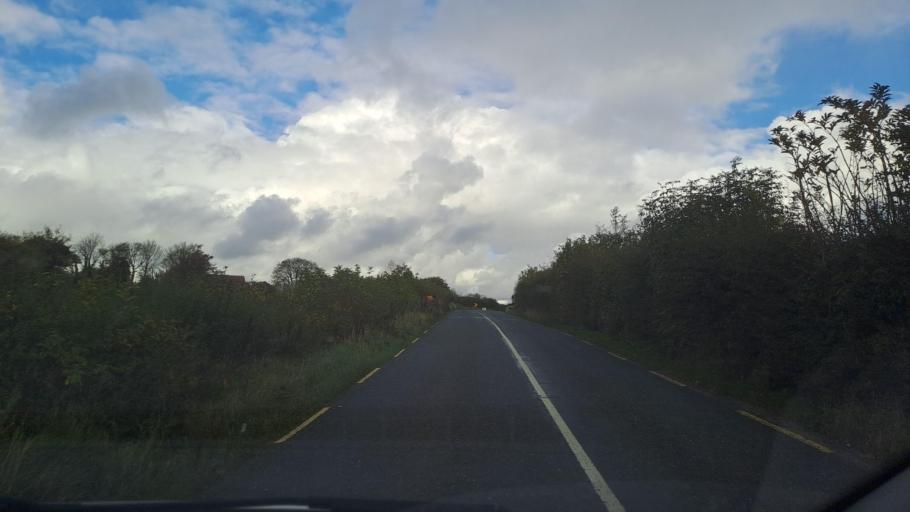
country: IE
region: Ulster
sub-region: An Cabhan
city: Mullagh
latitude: 53.8315
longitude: -6.9528
